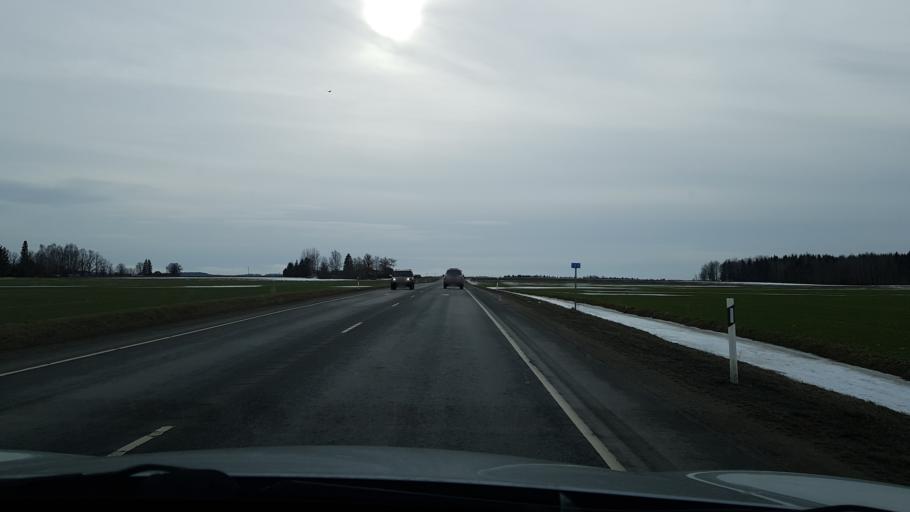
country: EE
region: Tartu
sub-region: UElenurme vald
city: Ulenurme
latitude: 58.2768
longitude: 26.7036
